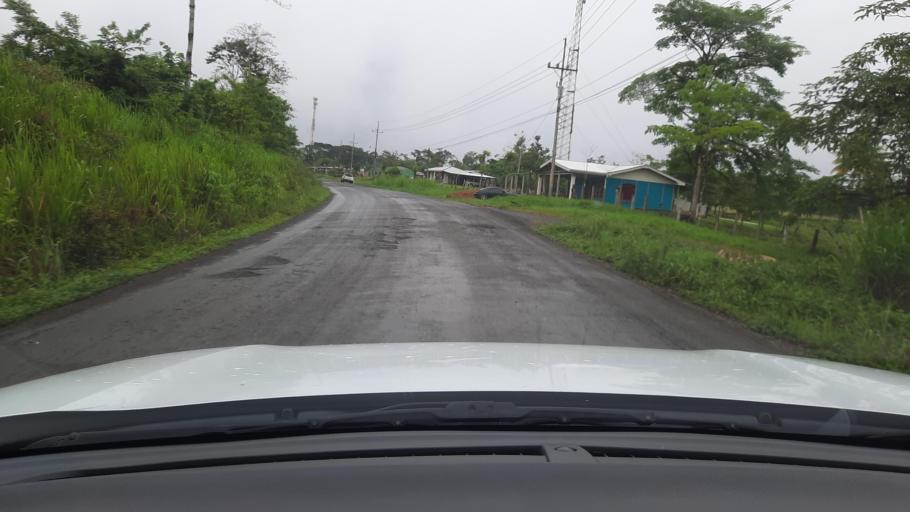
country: CR
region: Alajuela
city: San Jose
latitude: 11.0098
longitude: -85.3480
